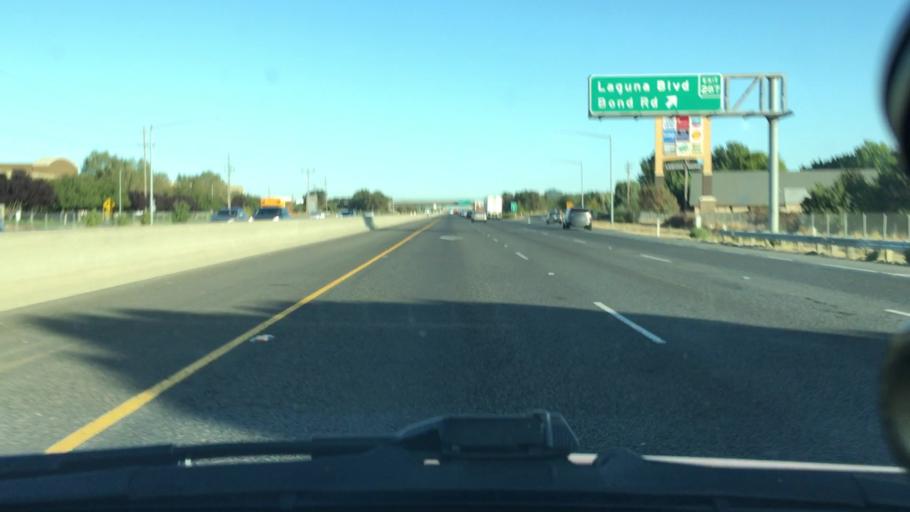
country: US
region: California
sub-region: Sacramento County
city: Elk Grove
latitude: 38.4188
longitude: -121.3931
